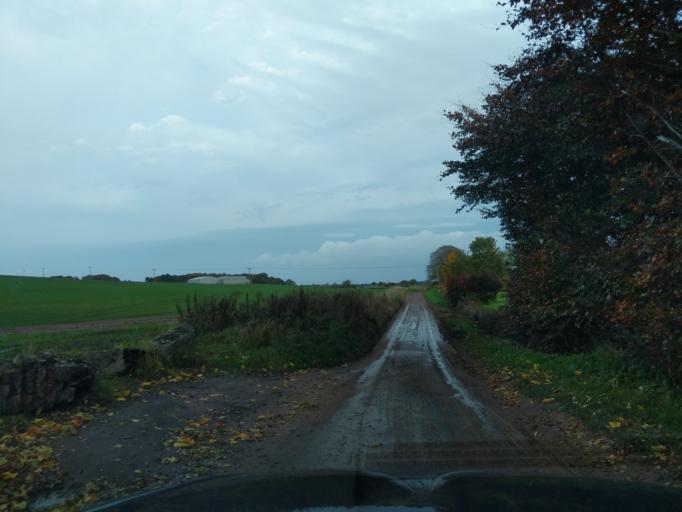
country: GB
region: Scotland
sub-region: Fife
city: Newport-On-Tay
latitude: 56.4240
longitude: -2.9084
